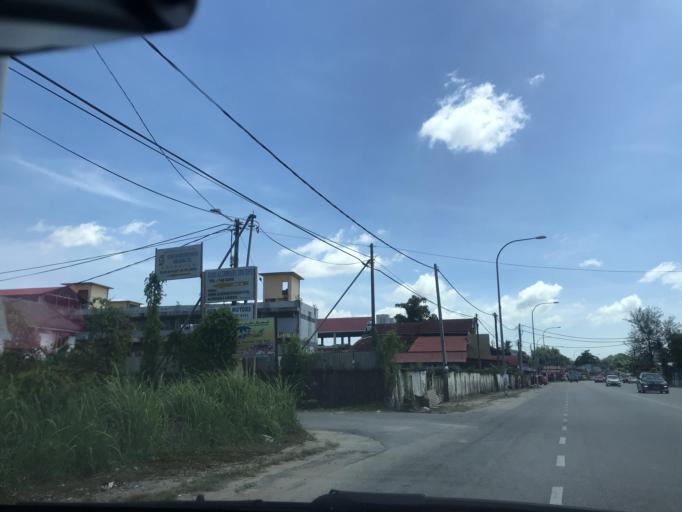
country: MY
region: Kelantan
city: Kota Bharu
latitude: 6.1084
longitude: 102.2632
